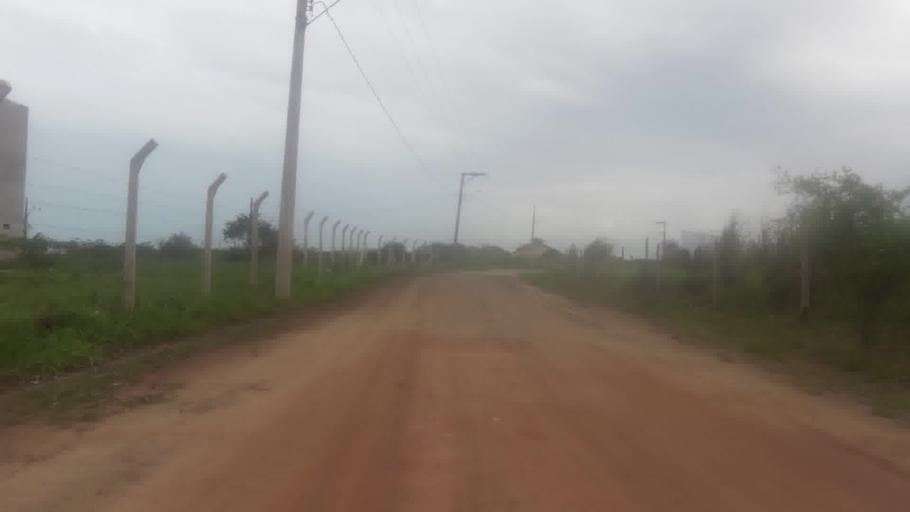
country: BR
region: Espirito Santo
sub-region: Piuma
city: Piuma
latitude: -20.7995
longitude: -40.5890
